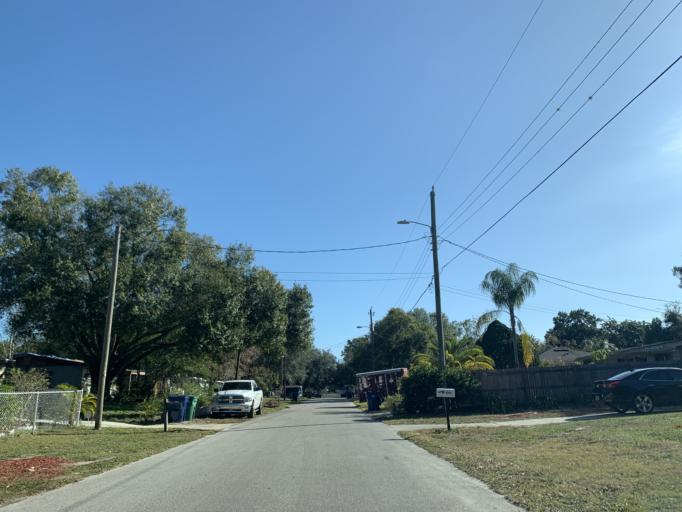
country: US
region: Florida
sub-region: Hillsborough County
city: Temple Terrace
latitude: 28.0275
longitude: -82.4133
